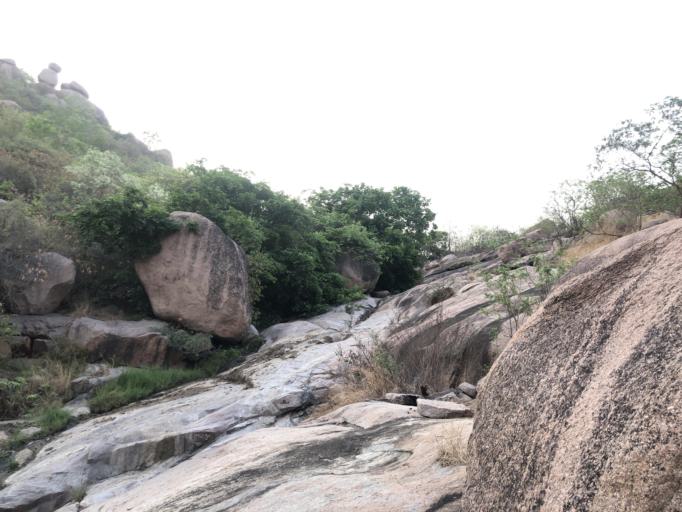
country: IN
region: Telangana
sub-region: Mahbubnagar
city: Farrukhnagar
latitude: 16.8921
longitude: 78.5012
